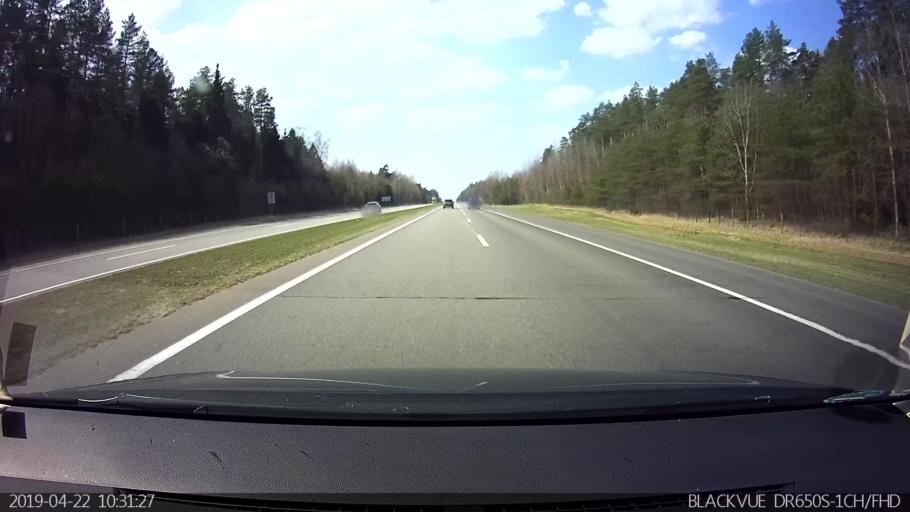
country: BY
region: Vitebsk
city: Talachyn
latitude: 54.4758
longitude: 29.7999
